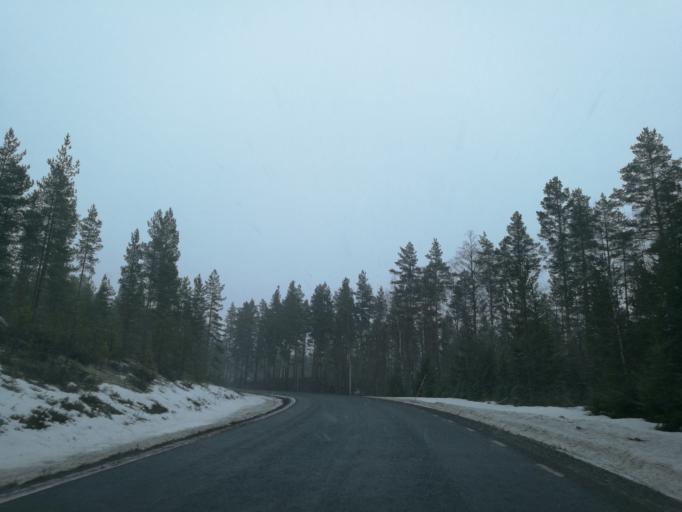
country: NO
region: Hedmark
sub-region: Grue
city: Kirkenaer
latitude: 60.6855
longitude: 12.6368
